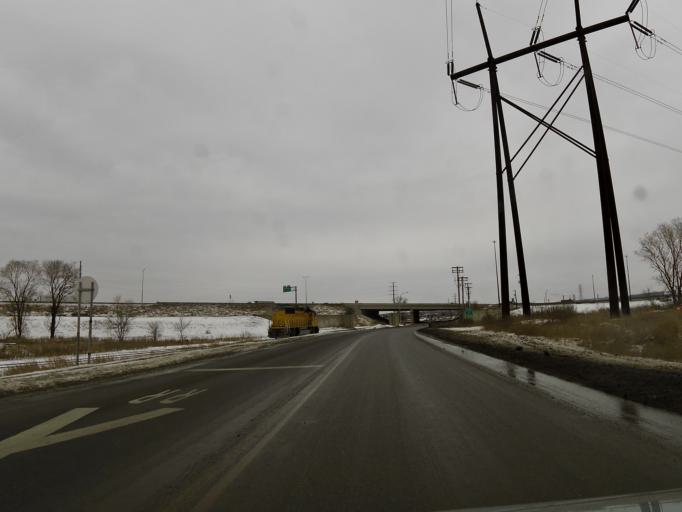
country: US
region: Minnesota
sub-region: Dakota County
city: South Saint Paul
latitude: 44.8777
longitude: -93.0244
